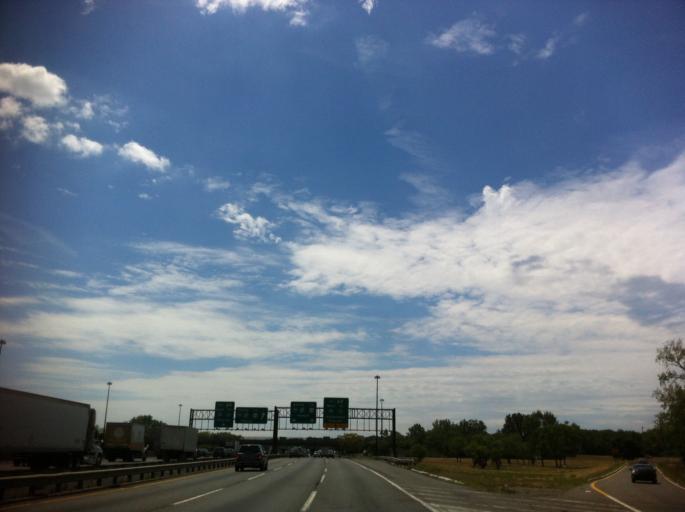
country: US
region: New Jersey
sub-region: Bergen County
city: Leonia
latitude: 40.8721
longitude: -73.9994
